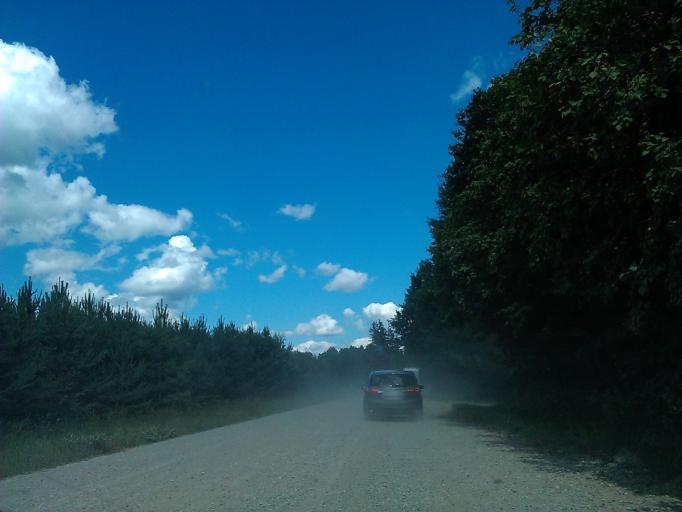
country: LV
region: Vilanu
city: Vilani
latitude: 56.5835
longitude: 26.9431
